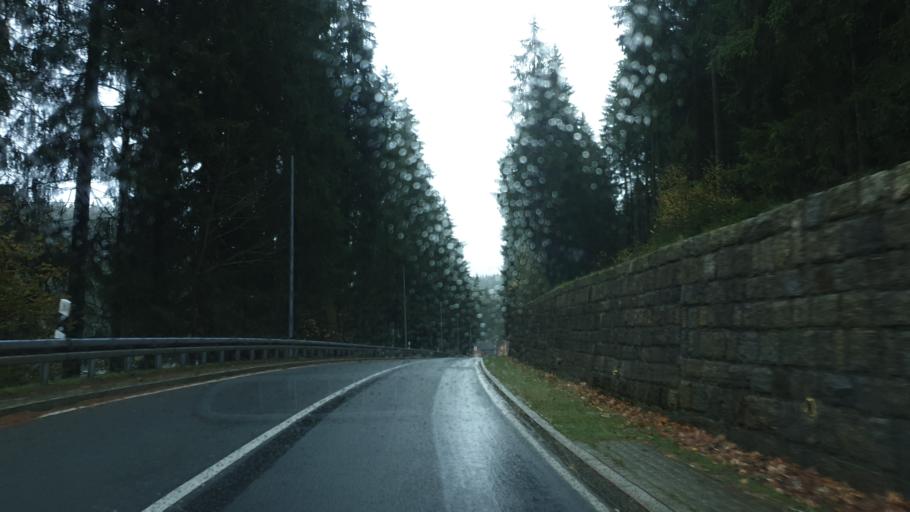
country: DE
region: Saxony
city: Schoenheide
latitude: 50.4760
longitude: 12.5126
